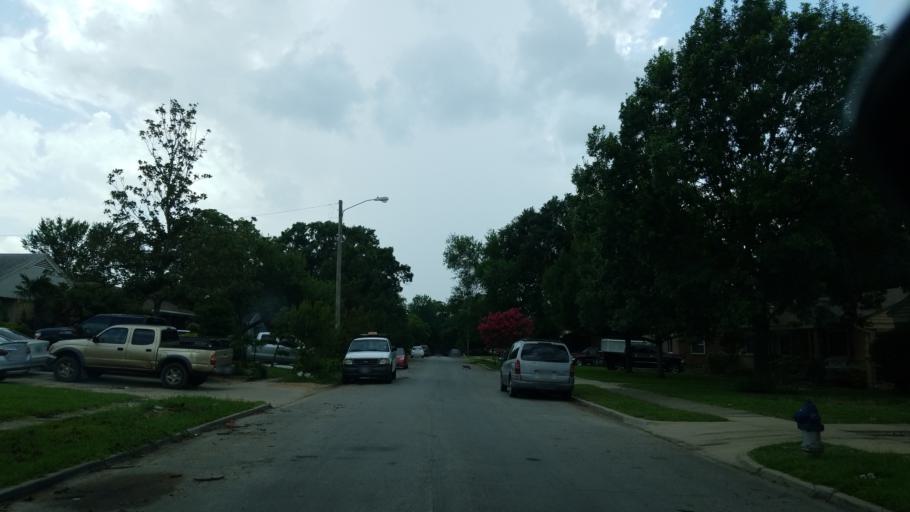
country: US
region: Texas
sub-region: Dallas County
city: Farmers Branch
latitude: 32.8797
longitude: -96.8599
